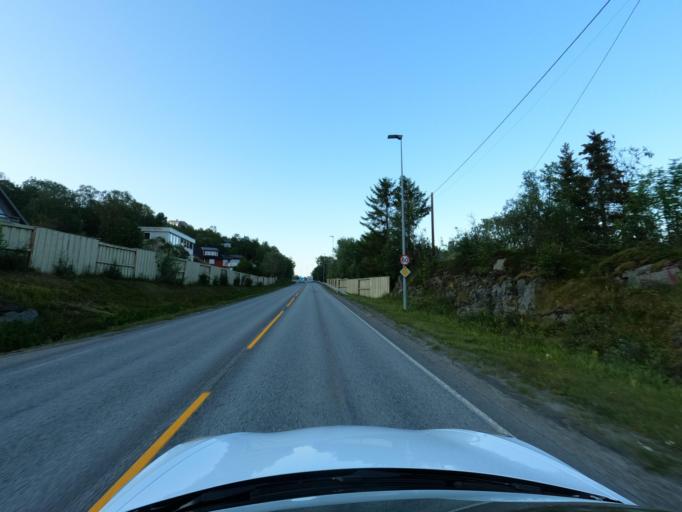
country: NO
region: Troms
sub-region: Harstad
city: Harstad
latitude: 68.7492
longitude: 16.5617
